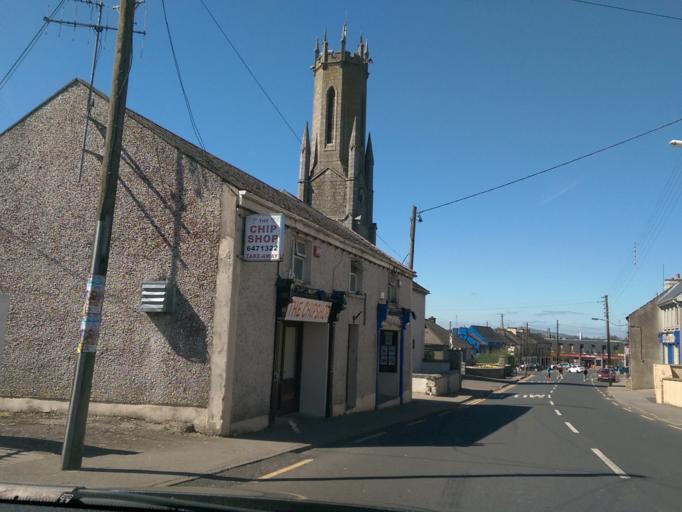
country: IE
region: Leinster
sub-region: Wicklow
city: Baltinglass
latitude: 52.8644
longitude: -6.5573
